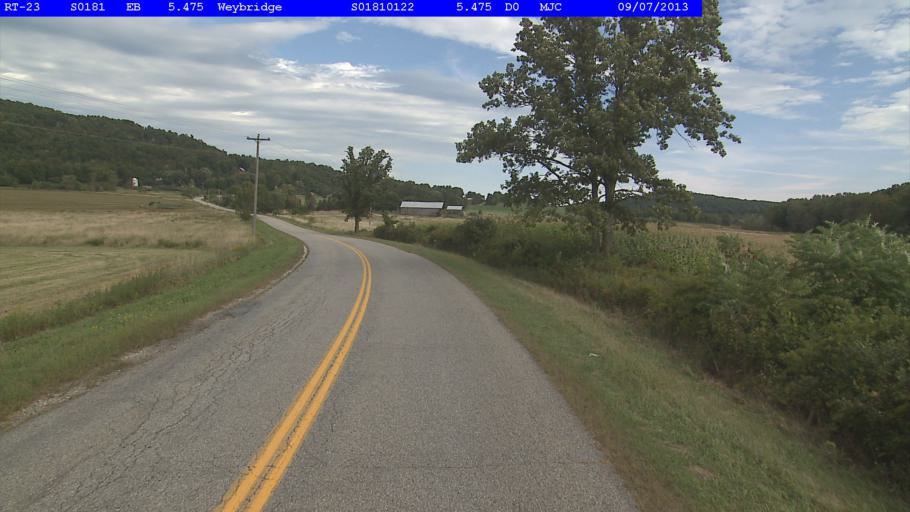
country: US
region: Vermont
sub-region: Addison County
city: Middlebury (village)
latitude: 44.0698
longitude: -73.2503
